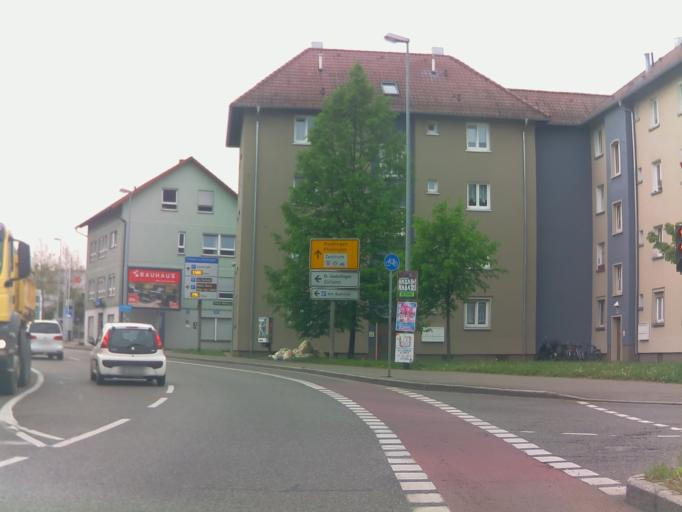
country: DE
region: Baden-Wuerttemberg
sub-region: Tuebingen Region
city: Reutlingen
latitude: 48.4973
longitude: 9.2050
